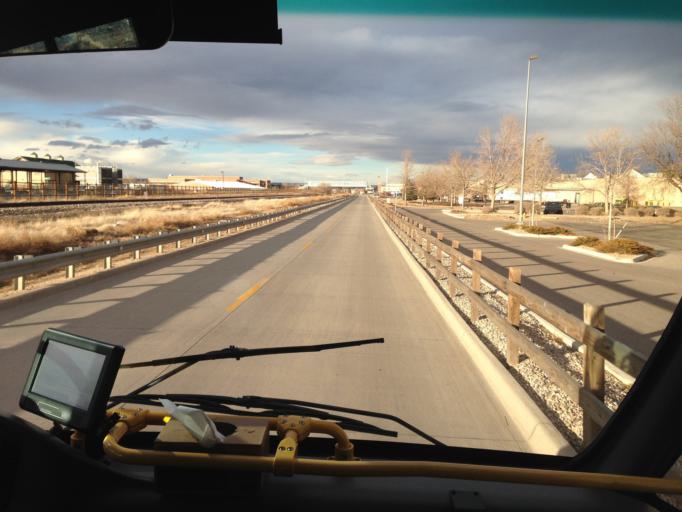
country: US
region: Colorado
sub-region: Larimer County
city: Fort Collins
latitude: 40.5550
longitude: -105.0797
